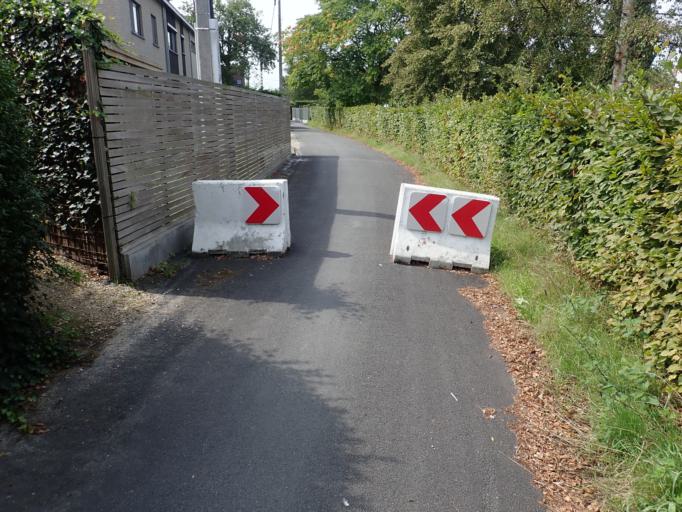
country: BE
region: Flanders
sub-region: Provincie Antwerpen
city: Bornem
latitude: 51.0879
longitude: 4.2211
